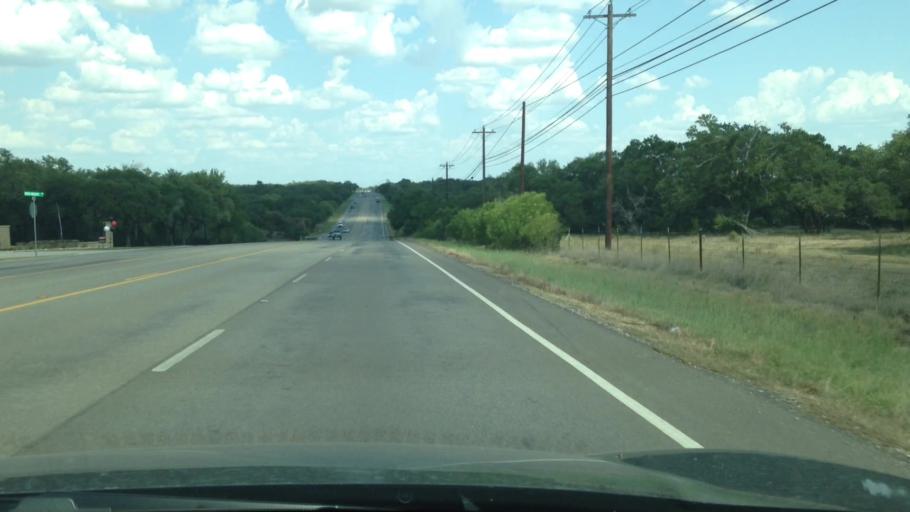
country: US
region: Texas
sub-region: Williamson County
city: Georgetown
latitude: 30.6336
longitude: -97.7727
